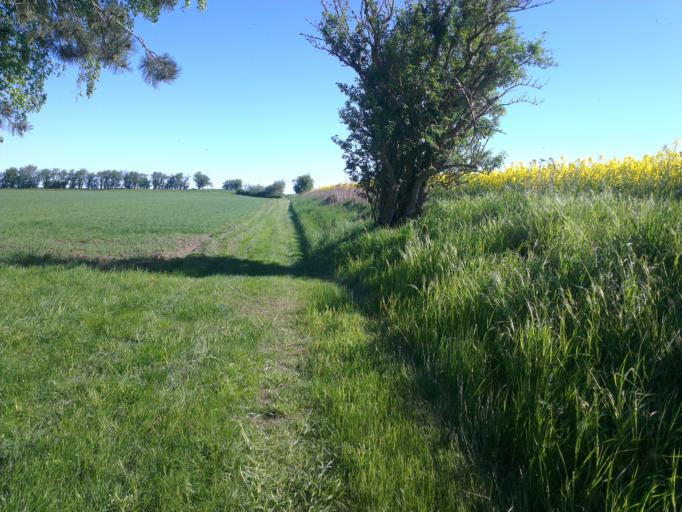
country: DK
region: Capital Region
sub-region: Frederikssund Kommune
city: Jaegerspris
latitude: 55.8400
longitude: 11.9766
